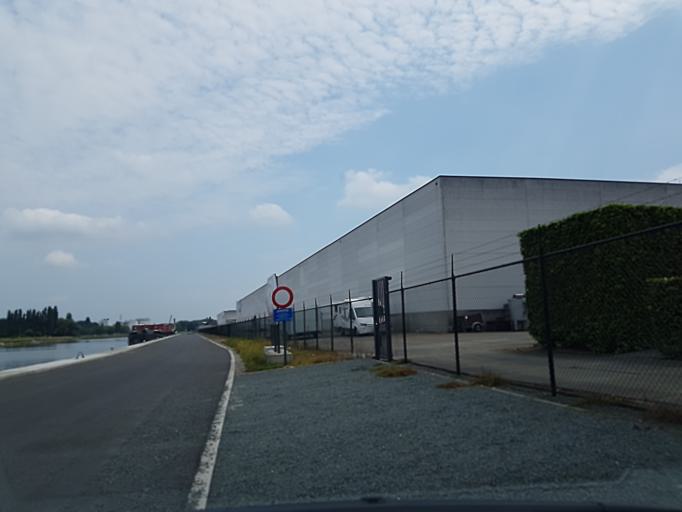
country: BE
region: Flanders
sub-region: Provincie Antwerpen
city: Schoten
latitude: 51.2396
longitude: 4.4773
